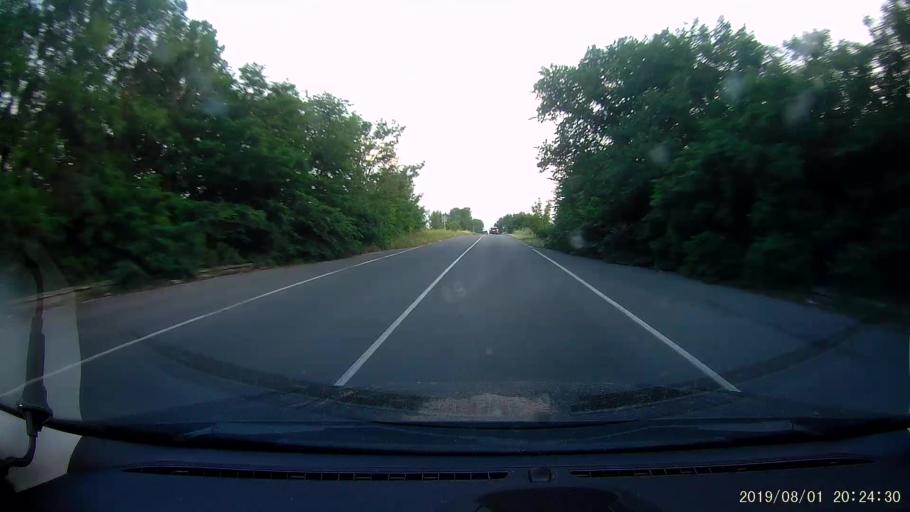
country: BG
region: Yambol
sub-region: Obshtina Elkhovo
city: Elkhovo
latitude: 42.2307
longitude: 26.5932
